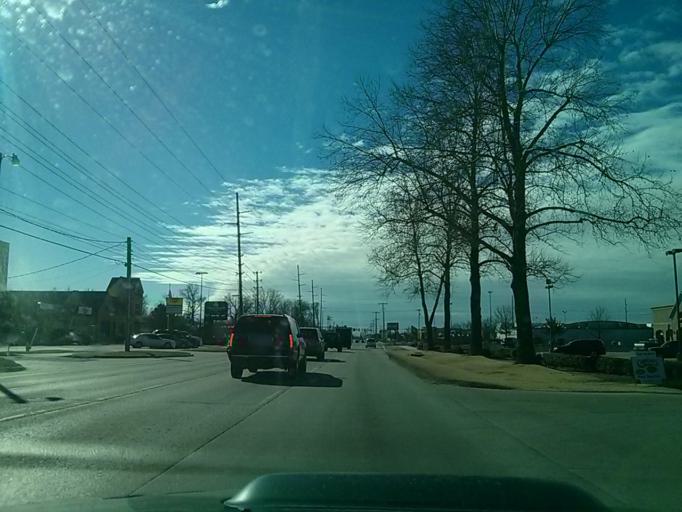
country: US
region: Oklahoma
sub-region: Tulsa County
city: Jenks
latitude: 36.0778
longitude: -95.9580
